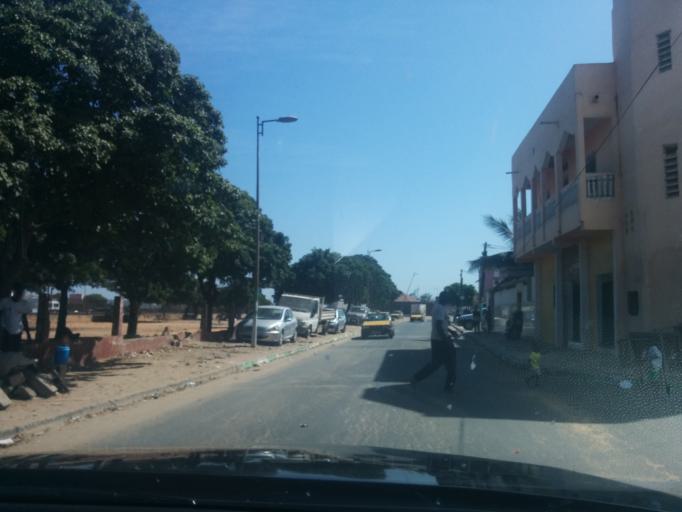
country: SN
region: Dakar
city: Grand Dakar
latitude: 14.7425
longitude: -17.4422
